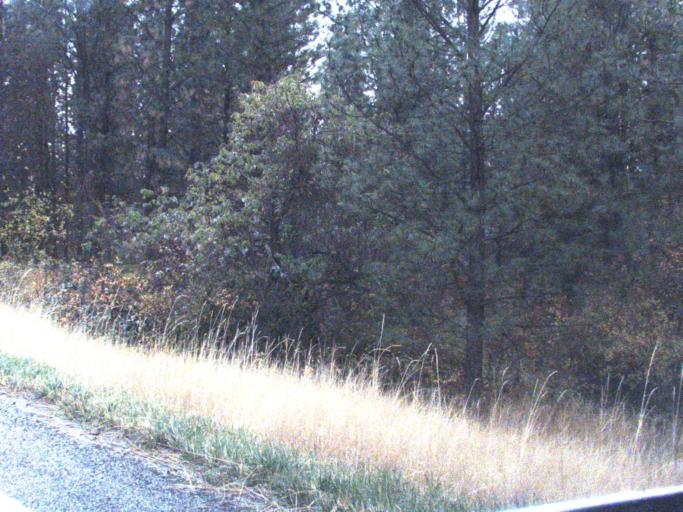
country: US
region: Washington
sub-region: Stevens County
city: Kettle Falls
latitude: 48.5128
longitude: -118.1460
